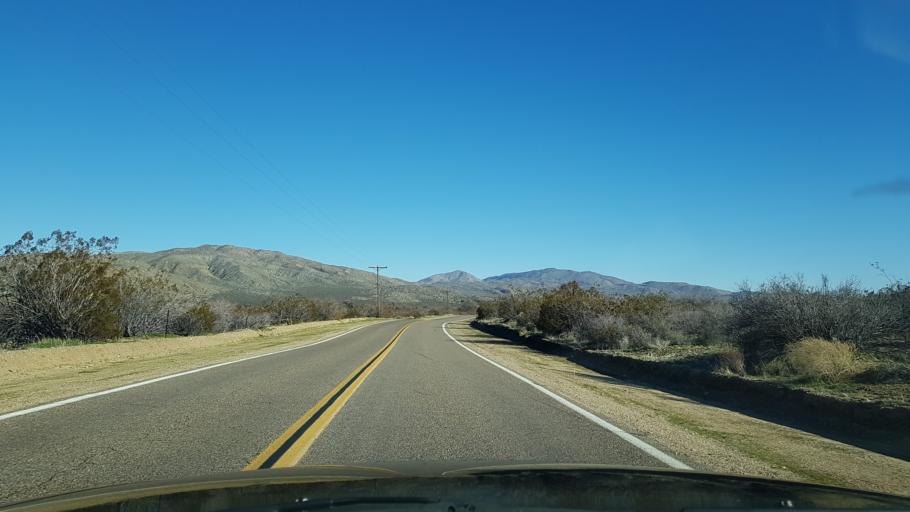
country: US
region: California
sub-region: San Diego County
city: Julian
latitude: 33.0942
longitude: -116.4648
